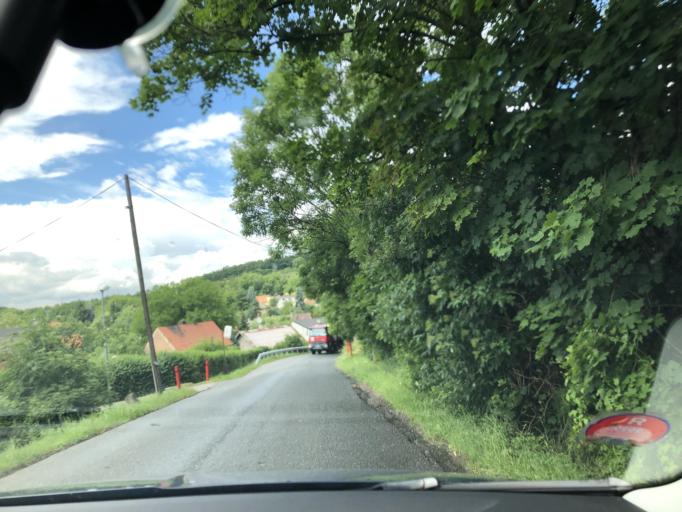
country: CZ
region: Central Bohemia
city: Nelahozeves
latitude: 50.2594
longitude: 14.2962
